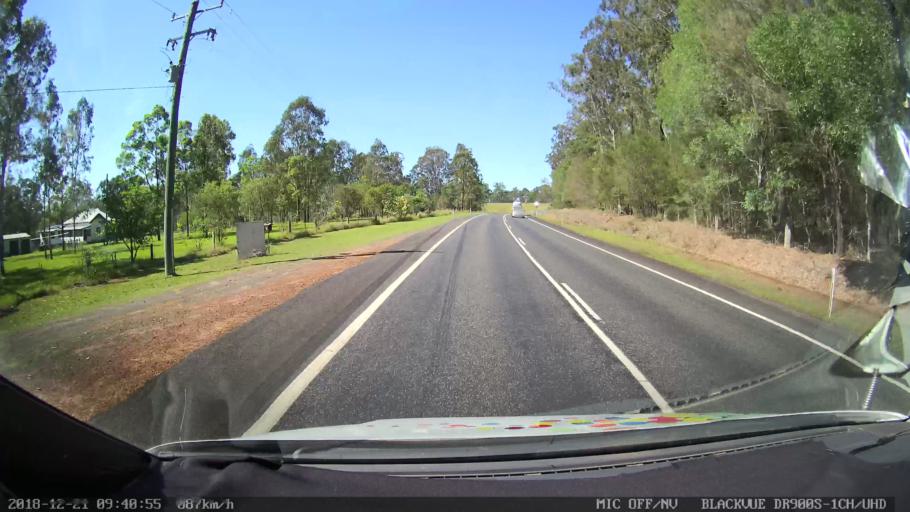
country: AU
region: New South Wales
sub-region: Clarence Valley
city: Grafton
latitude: -29.5791
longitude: 152.9618
